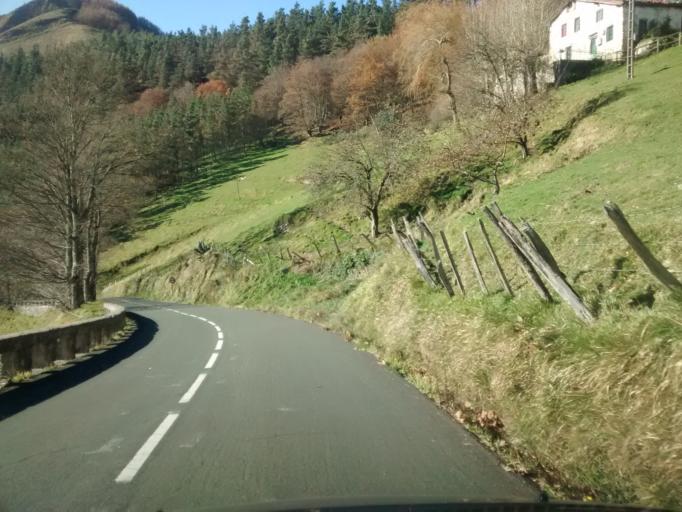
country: ES
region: Basque Country
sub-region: Provincia de Guipuzcoa
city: Eibar
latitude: 43.2063
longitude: -2.4758
